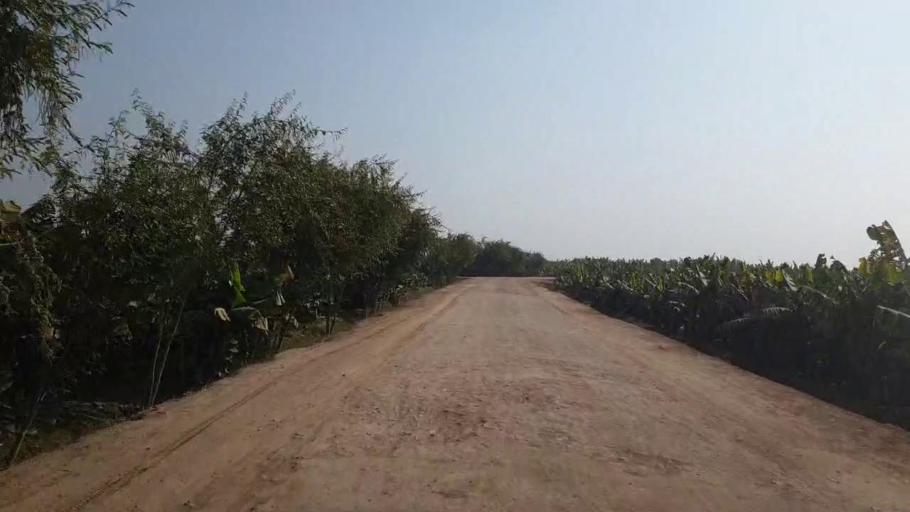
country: PK
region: Sindh
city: Bhit Shah
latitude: 25.7912
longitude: 68.4970
